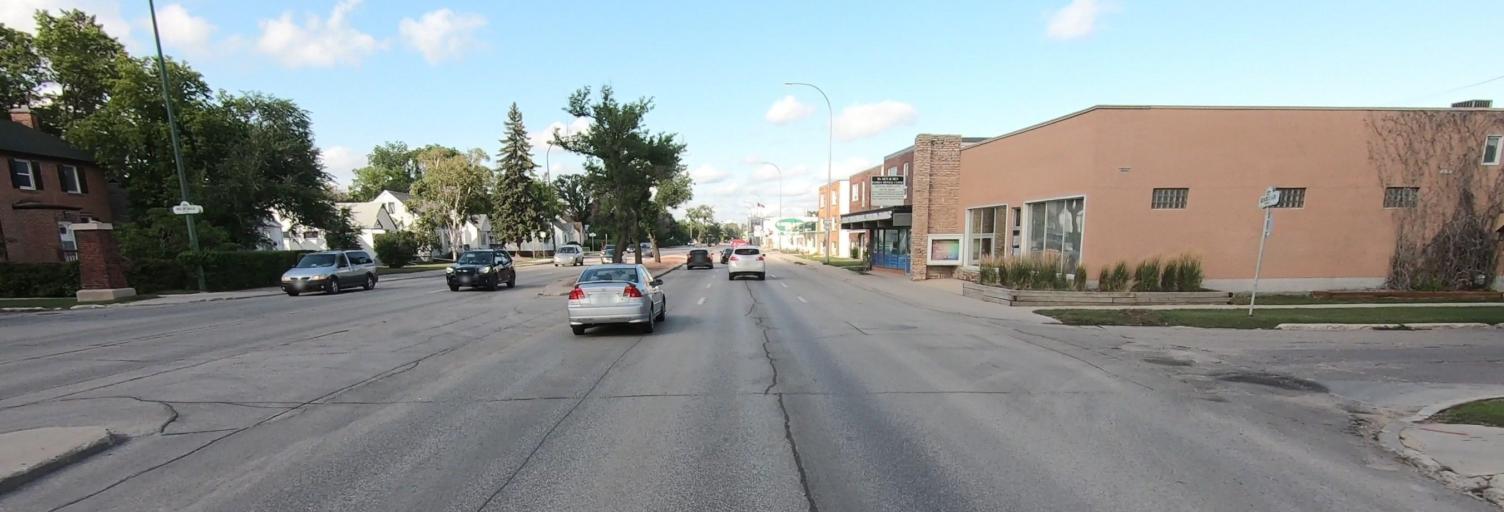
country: CA
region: Manitoba
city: Winnipeg
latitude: 49.9283
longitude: -97.1032
